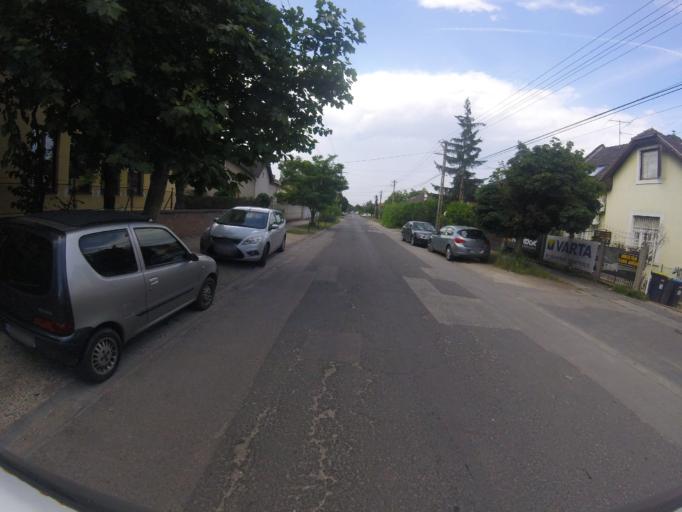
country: HU
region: Budapest
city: Budapest XXI. keruelet
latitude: 47.4193
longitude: 19.0777
